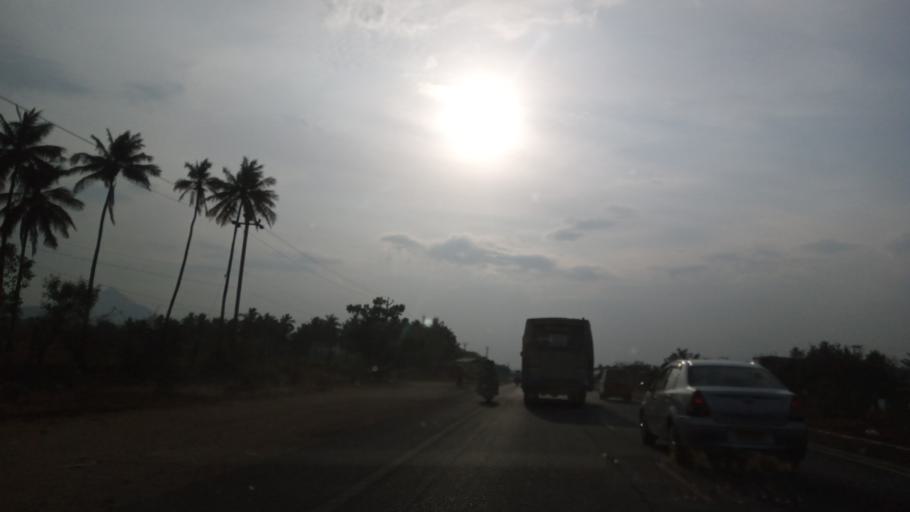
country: IN
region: Tamil Nadu
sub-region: Salem
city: Belur
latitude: 11.6649
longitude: 78.2970
